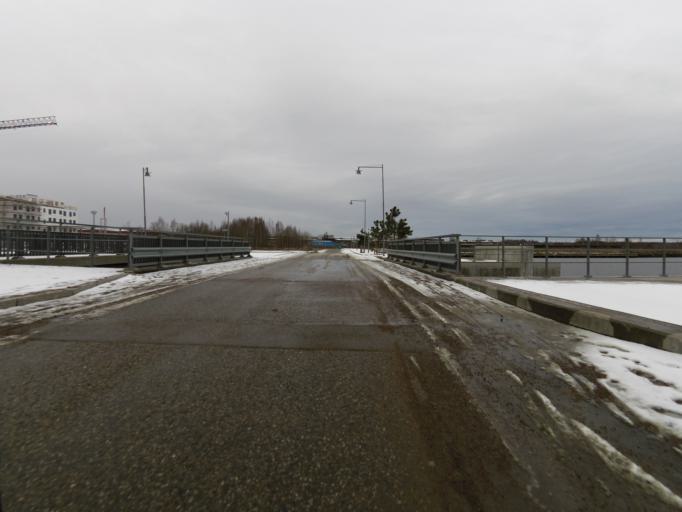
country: SE
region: Gaevleborg
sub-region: Gavle Kommun
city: Gavle
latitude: 60.6808
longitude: 17.1712
